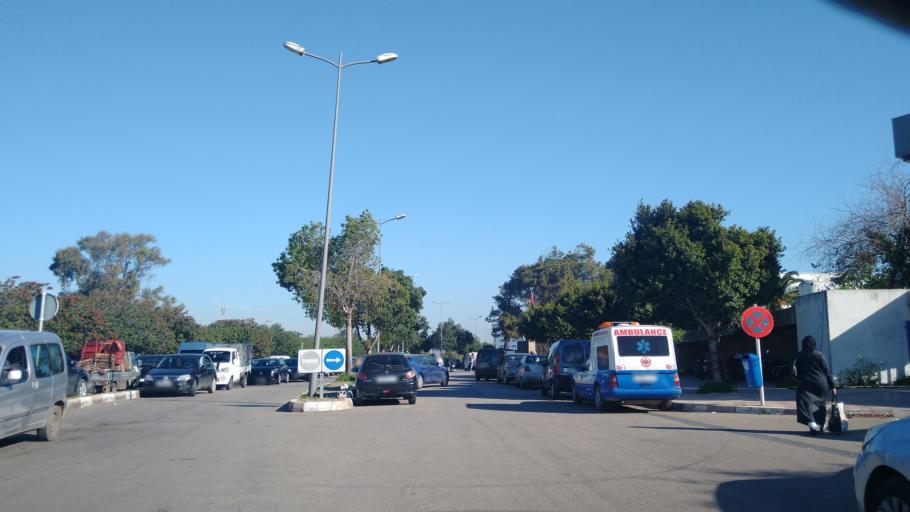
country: MA
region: Rabat-Sale-Zemmour-Zaer
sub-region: Rabat
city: Rabat
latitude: 33.9840
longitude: -6.8532
